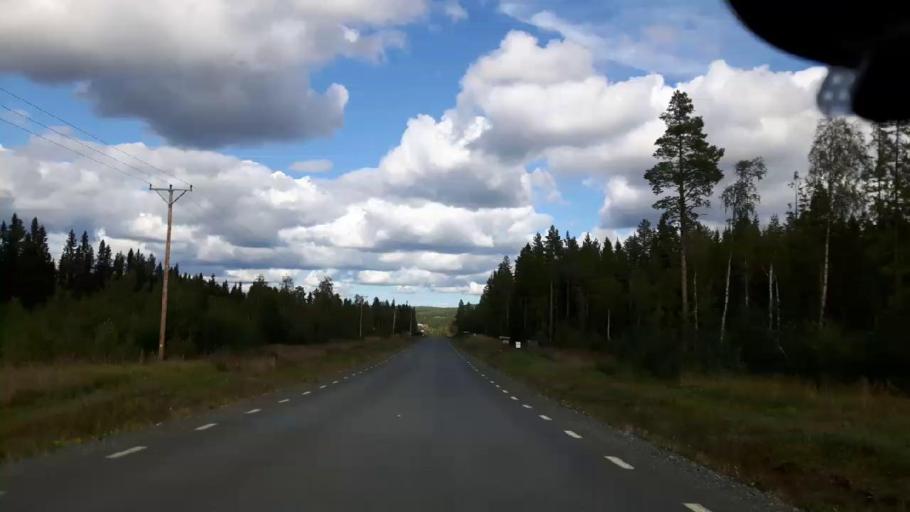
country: SE
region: Jaemtland
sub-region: Braecke Kommun
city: Braecke
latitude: 63.2847
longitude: 15.5829
